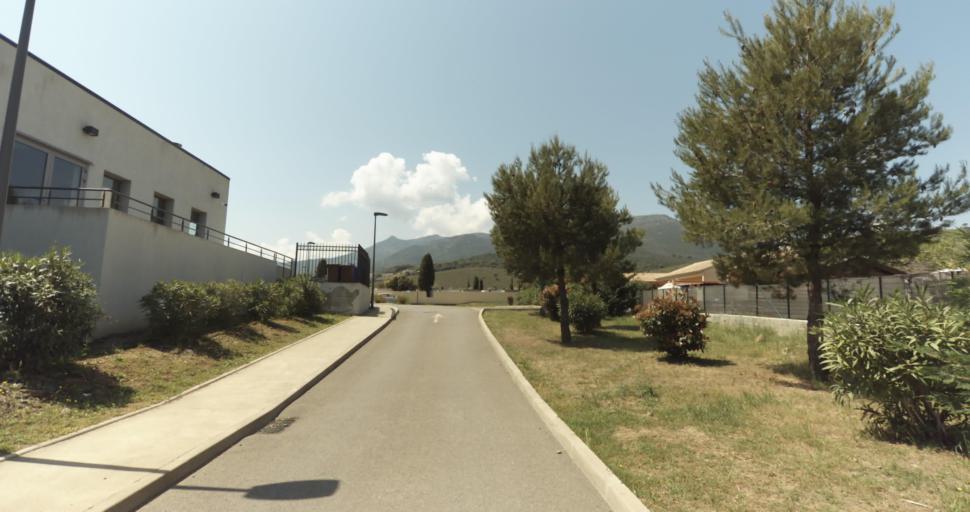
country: FR
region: Corsica
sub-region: Departement de la Haute-Corse
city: Biguglia
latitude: 42.6006
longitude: 9.4333
